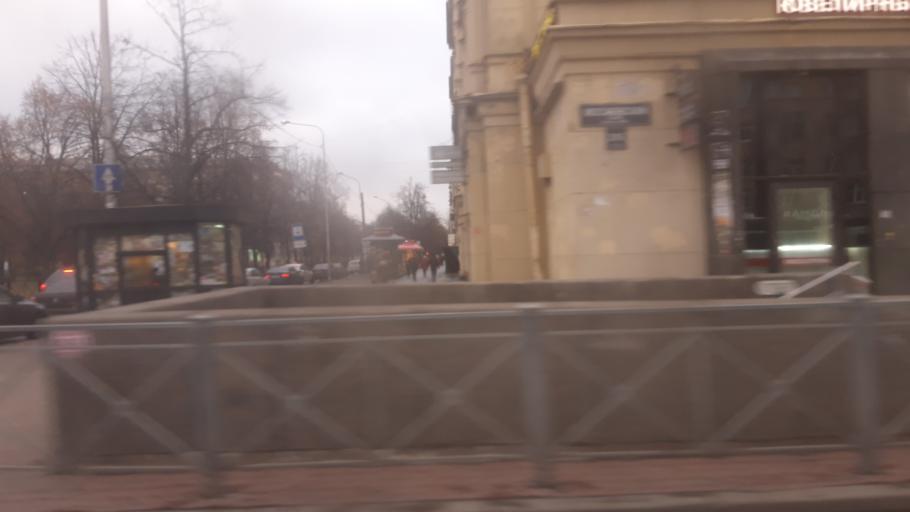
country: RU
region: St.-Petersburg
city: Kupchino
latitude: 59.8491
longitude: 30.3218
